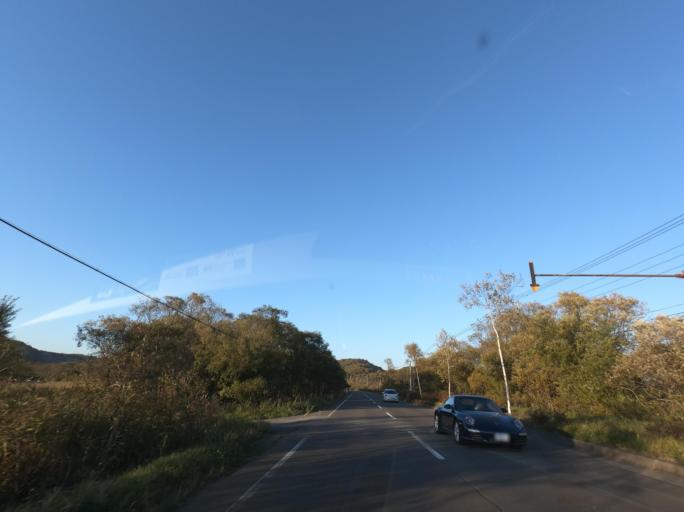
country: JP
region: Hokkaido
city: Kushiro
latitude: 43.0632
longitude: 144.2975
